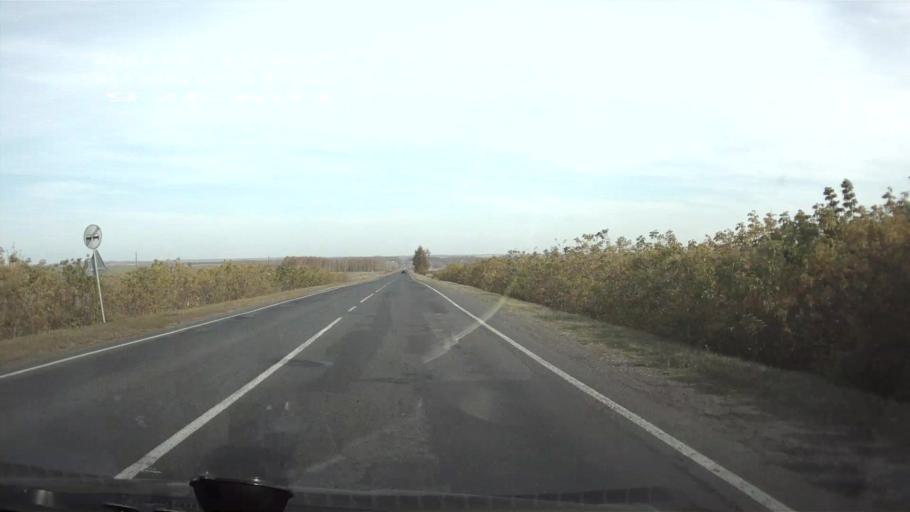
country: RU
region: Mordoviya
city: Atyashevo
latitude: 54.5389
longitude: 45.9313
